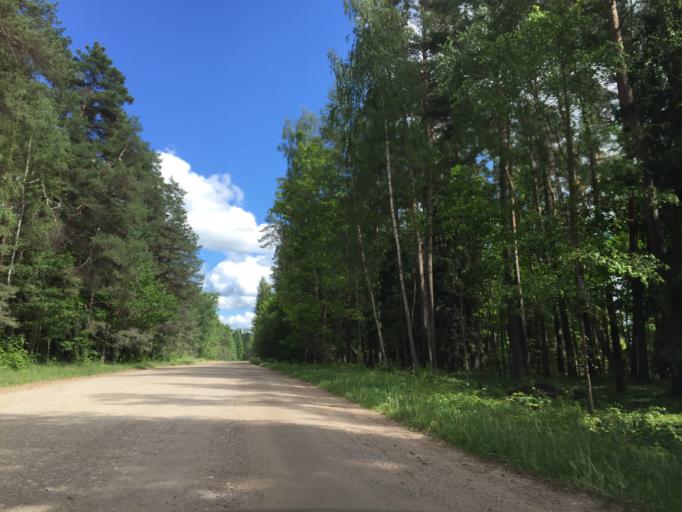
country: LV
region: Lecava
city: Iecava
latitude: 56.5747
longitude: 24.3192
